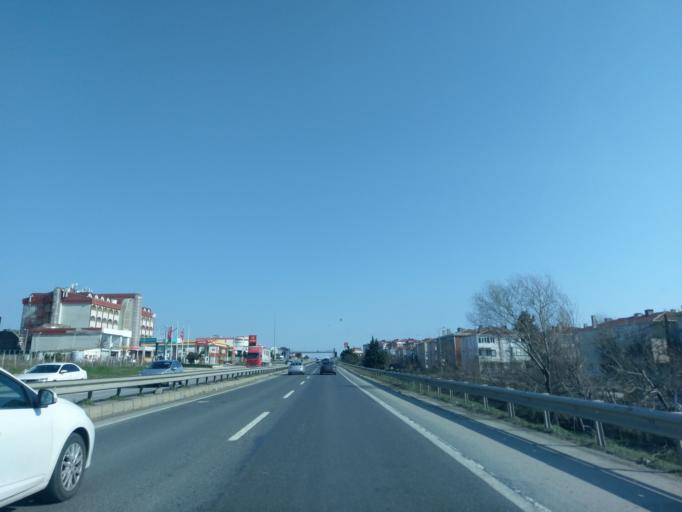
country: TR
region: Istanbul
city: Selimpasa
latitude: 41.0518
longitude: 28.3852
